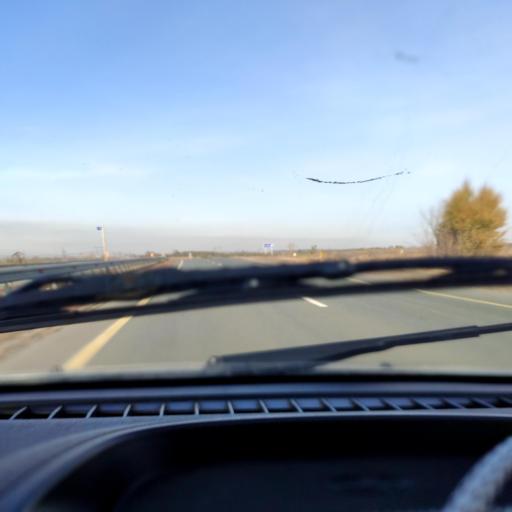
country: RU
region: Samara
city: Zhigulevsk
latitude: 53.5126
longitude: 49.5377
